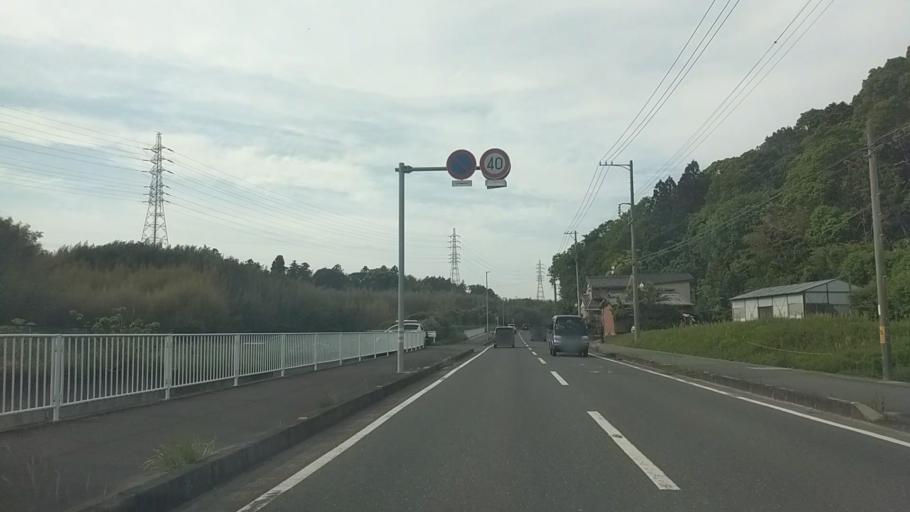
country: JP
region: Shizuoka
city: Hamamatsu
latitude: 34.7481
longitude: 137.6542
